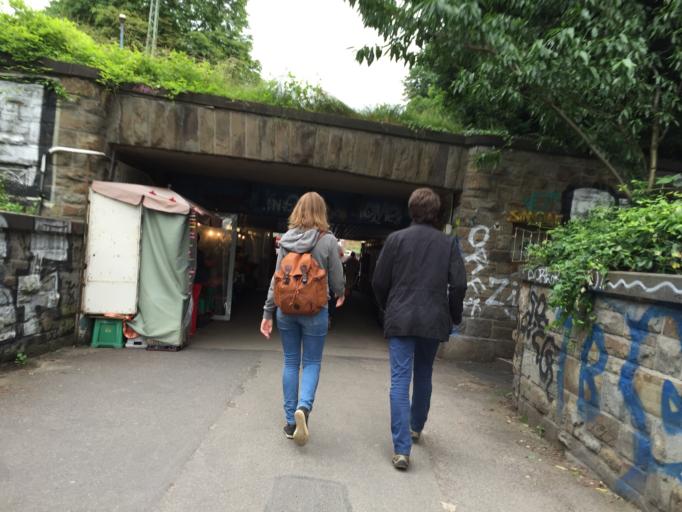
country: DE
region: North Rhine-Westphalia
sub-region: Regierungsbezirk Koln
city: Bonn
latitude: 50.7310
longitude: 7.0997
